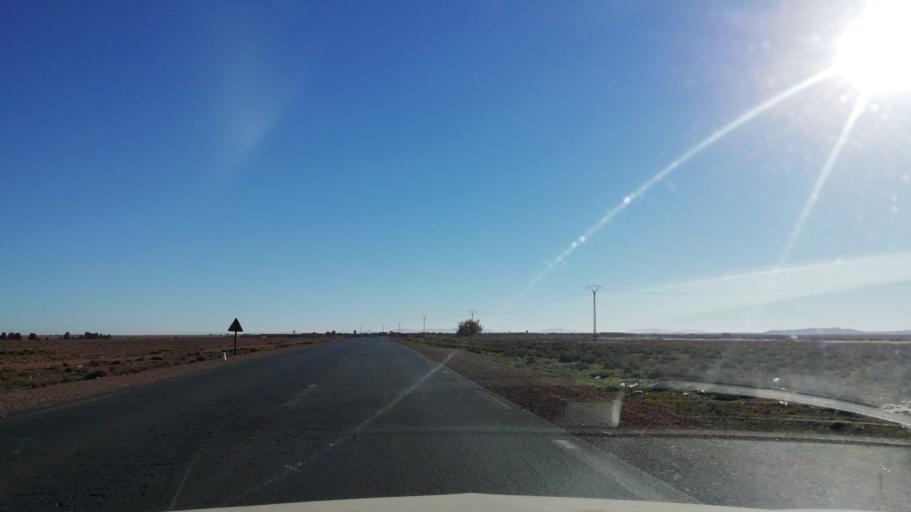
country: DZ
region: El Bayadh
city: El Bayadh
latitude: 33.8542
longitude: 0.6090
